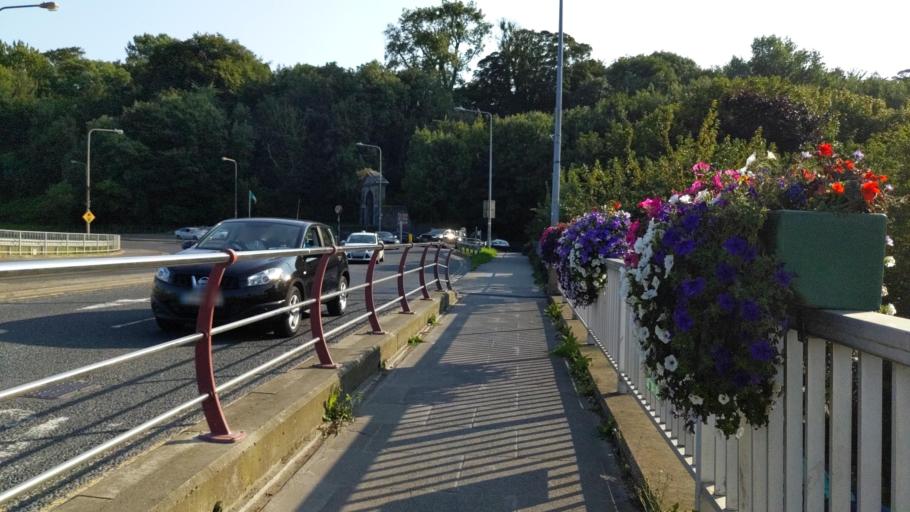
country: IE
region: Leinster
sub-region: Lu
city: Drogheda
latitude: 53.7147
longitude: -6.3584
